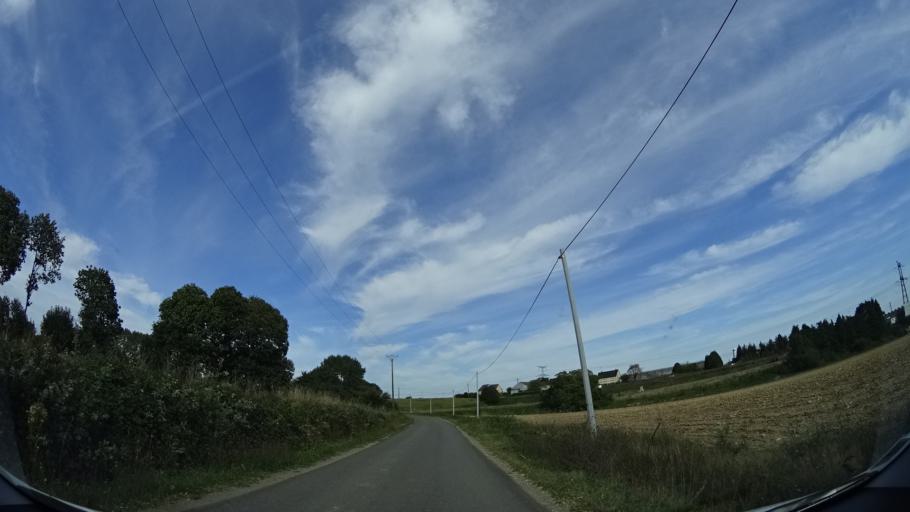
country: FR
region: Brittany
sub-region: Departement d'Ille-et-Vilaine
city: Romagne
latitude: 48.3209
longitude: -1.2742
